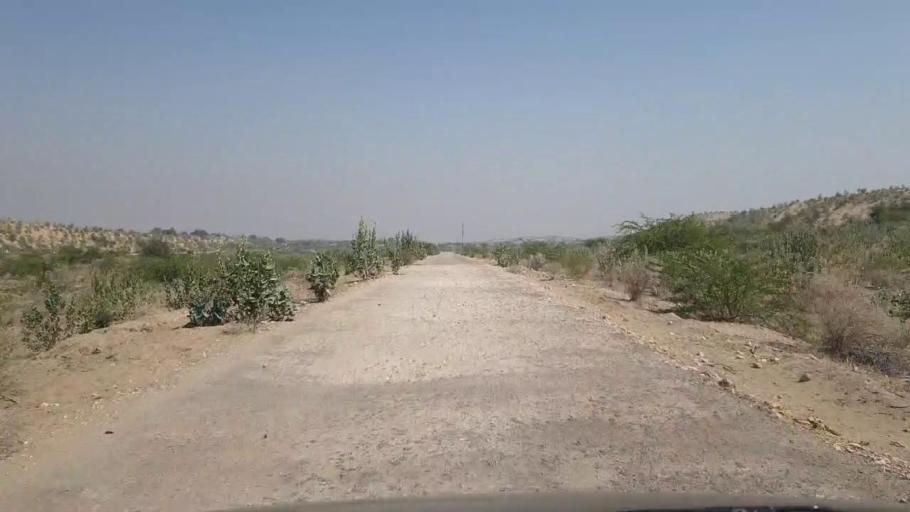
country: PK
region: Sindh
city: Chor
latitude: 25.6888
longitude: 70.1862
